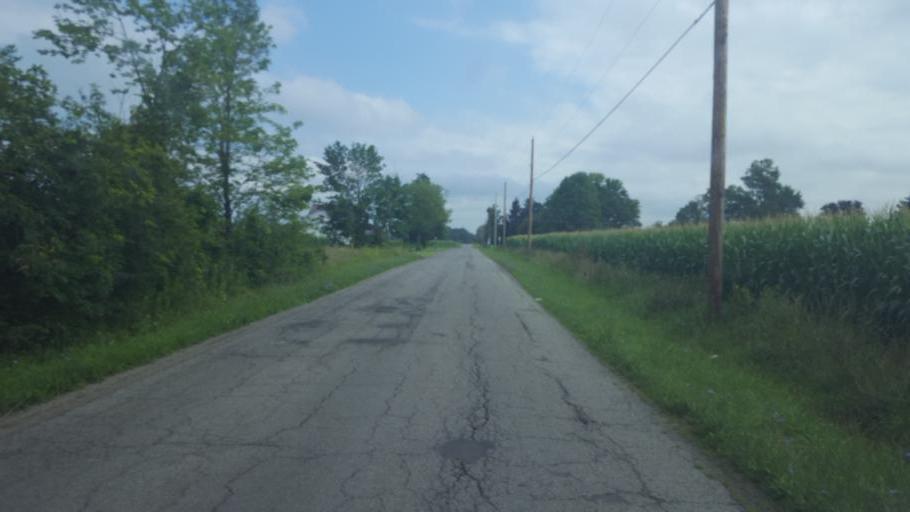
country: US
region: Ohio
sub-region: Crawford County
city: Galion
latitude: 40.6960
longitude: -82.7839
